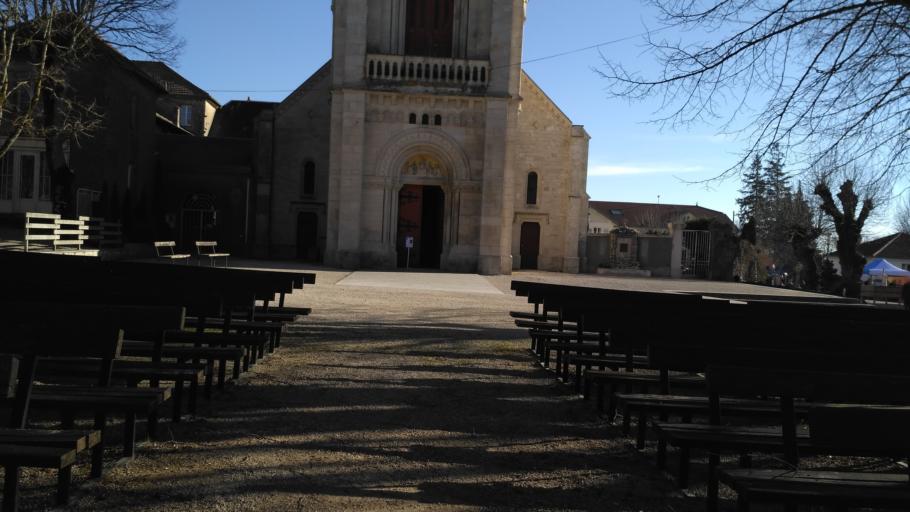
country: FR
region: Lorraine
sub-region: Departement de Meurthe-et-Moselle
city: Vezelise
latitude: 48.4311
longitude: 6.0833
